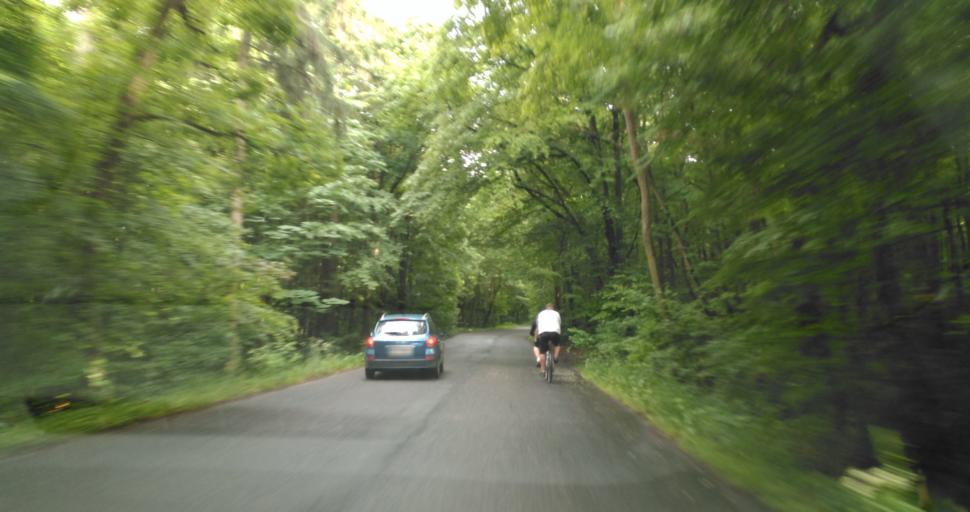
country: CZ
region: Central Bohemia
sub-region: Okres Beroun
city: Beroun
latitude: 49.9049
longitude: 14.0779
